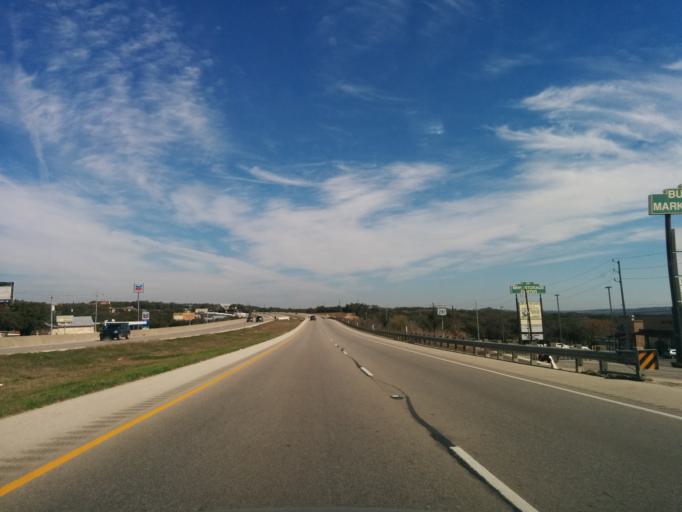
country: US
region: Texas
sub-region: Comal County
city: Bulverde
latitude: 29.7409
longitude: -98.4367
